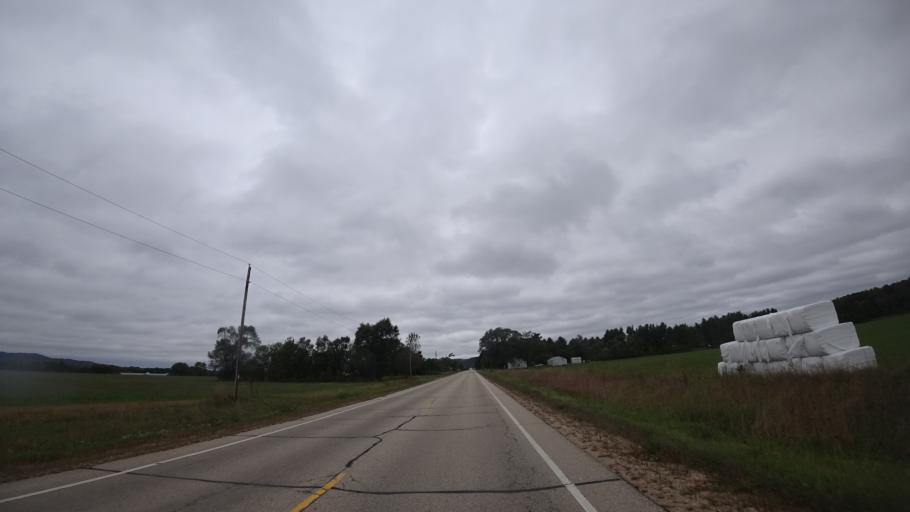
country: US
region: Wisconsin
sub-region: Grant County
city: Boscobel
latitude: 43.2054
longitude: -90.6035
